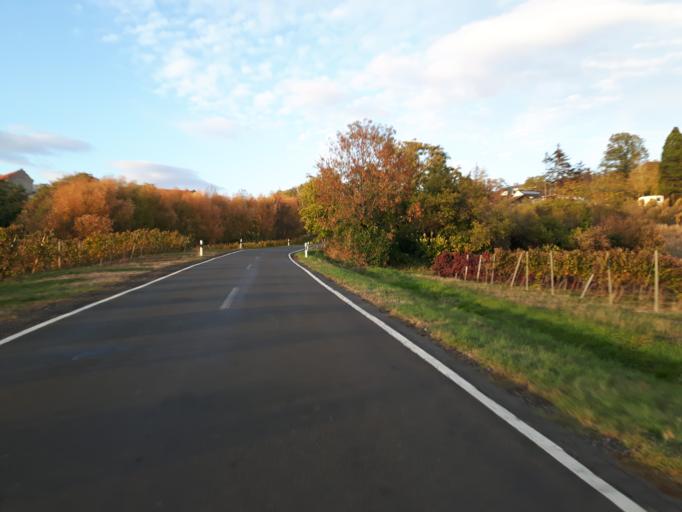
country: DE
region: Rheinland-Pfalz
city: Molsheim
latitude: 49.6437
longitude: 8.1703
